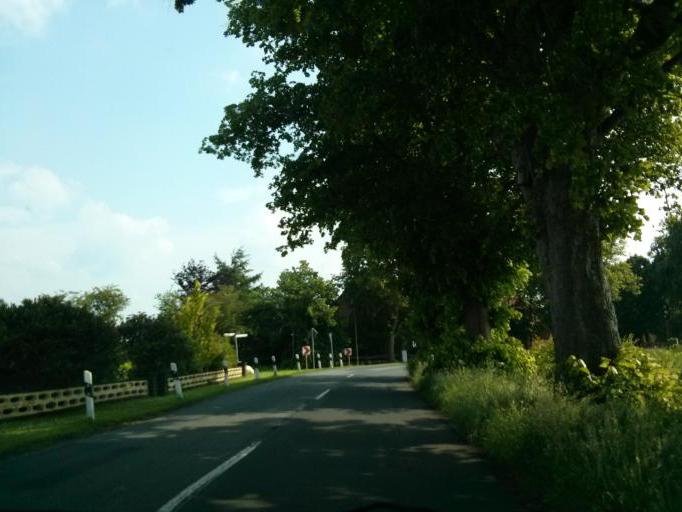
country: DE
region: Lower Saxony
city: Lunestedt
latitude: 53.4990
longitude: 8.7205
